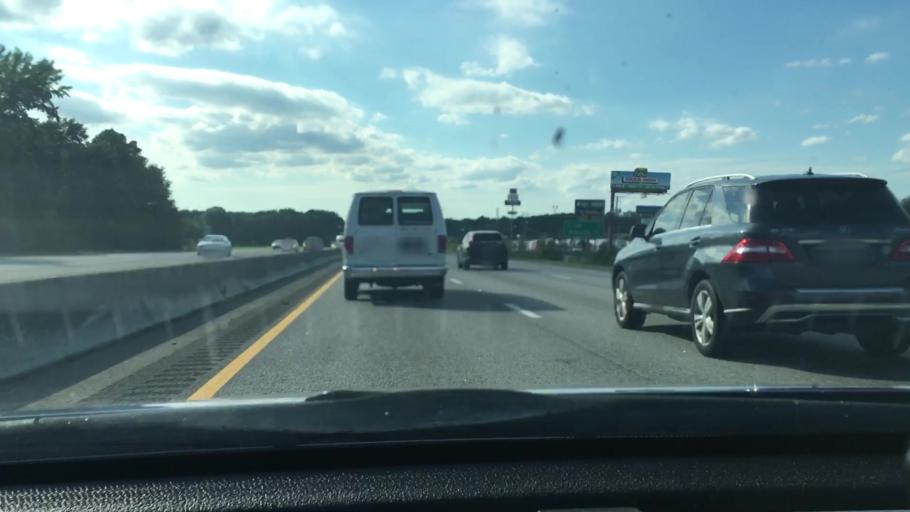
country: US
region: South Carolina
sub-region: Richland County
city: Dentsville
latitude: 34.0735
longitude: -80.9932
